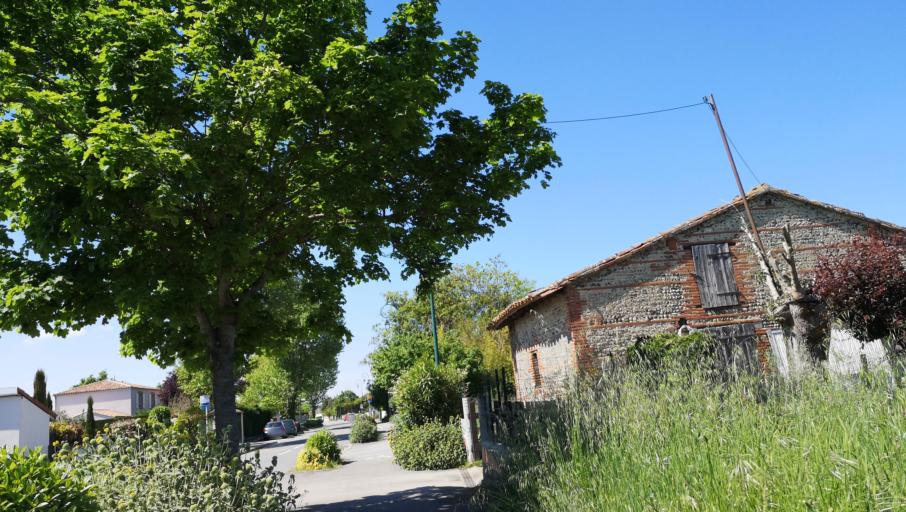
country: FR
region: Midi-Pyrenees
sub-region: Departement de la Haute-Garonne
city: Seilh
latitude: 43.6836
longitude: 1.3653
